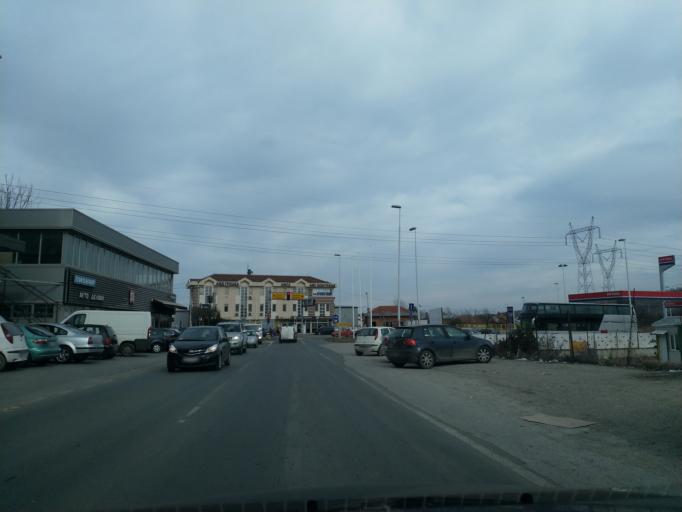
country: RS
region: Central Serbia
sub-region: Belgrade
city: Zvezdara
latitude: 44.7442
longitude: 20.6000
